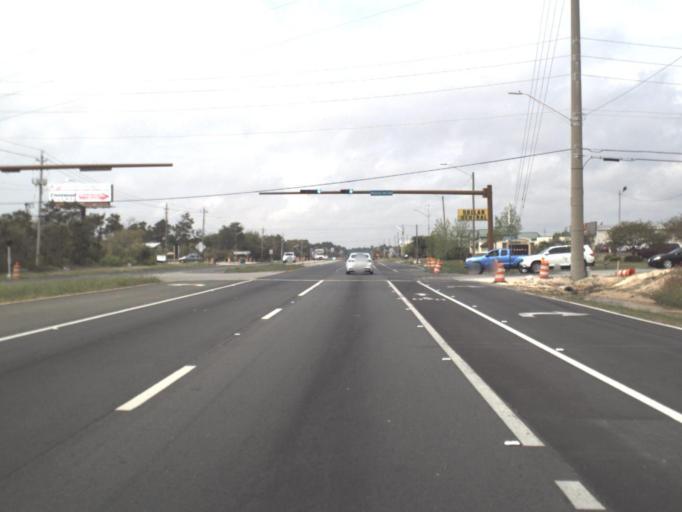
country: US
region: Florida
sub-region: Santa Rosa County
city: Navarre
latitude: 30.4097
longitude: -86.8201
